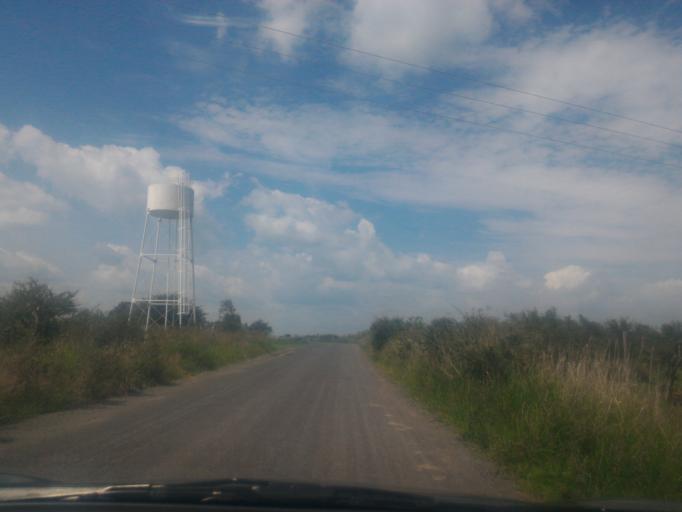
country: MX
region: Guanajuato
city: Ciudad Manuel Doblado
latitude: 20.8097
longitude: -102.0694
